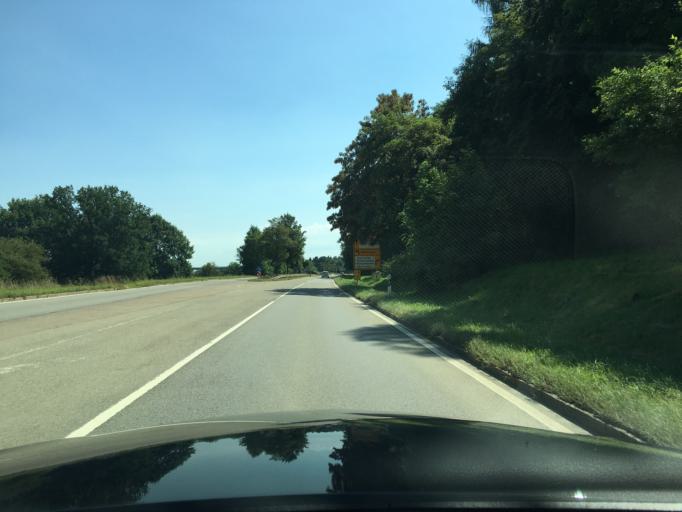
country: DE
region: Baden-Wuerttemberg
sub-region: Tuebingen Region
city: Dornstadt
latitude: 48.4278
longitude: 9.9526
